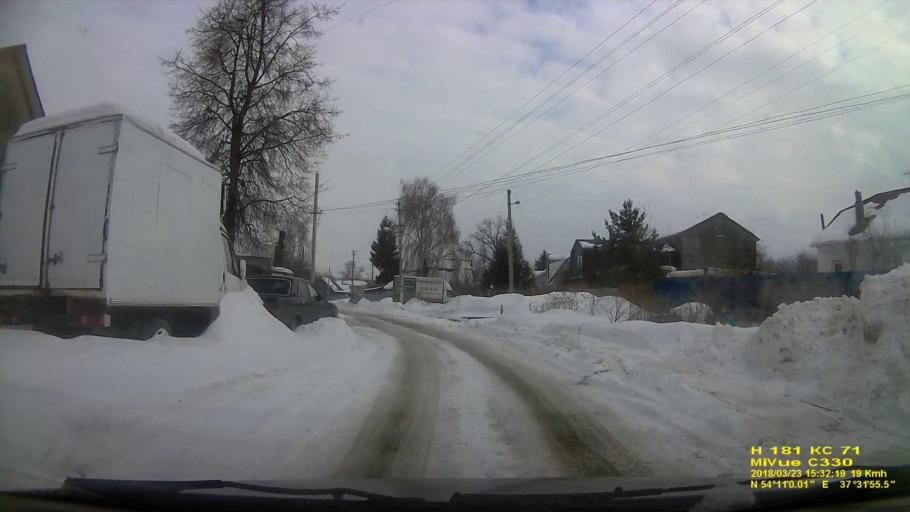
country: RU
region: Tula
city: Kosaya Gora
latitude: 54.1833
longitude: 37.5321
